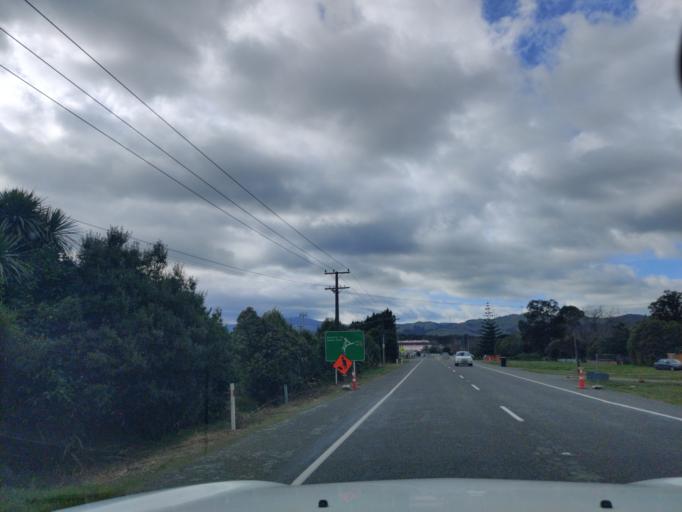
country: NZ
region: Manawatu-Wanganui
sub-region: Palmerston North City
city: Palmerston North
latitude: -40.2990
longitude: 175.7456
